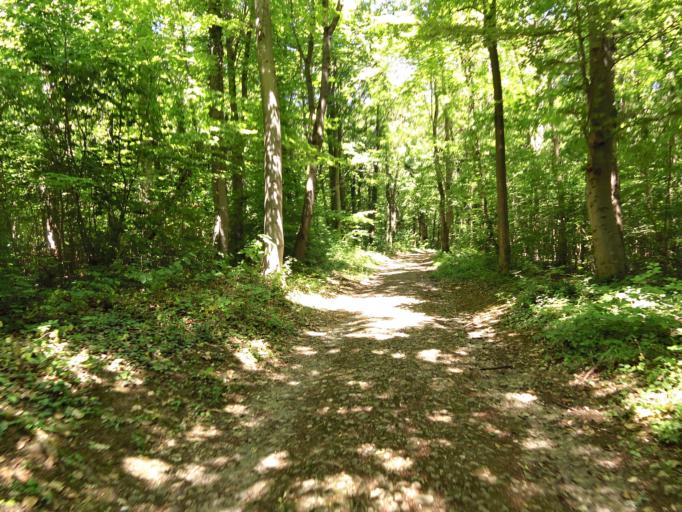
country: DE
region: Bavaria
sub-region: Regierungsbezirk Unterfranken
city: Hochberg
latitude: 49.7807
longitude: 9.9168
